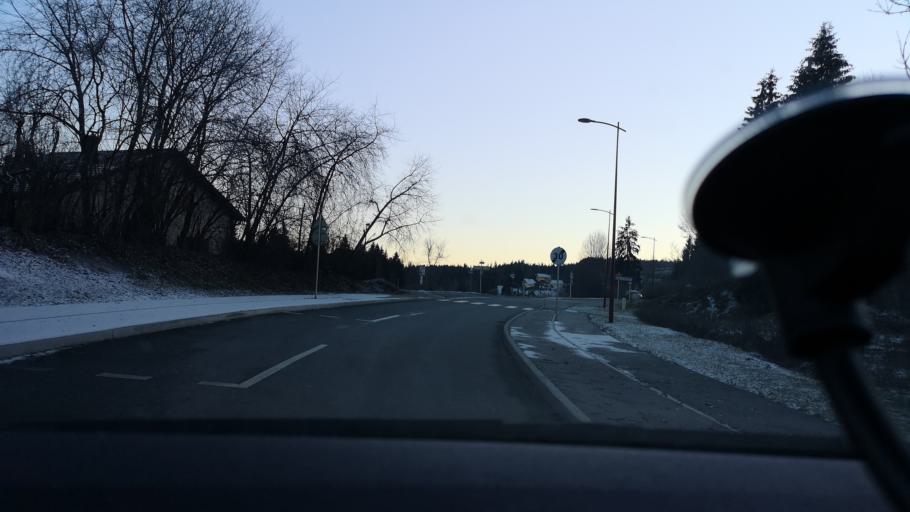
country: FR
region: Franche-Comte
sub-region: Departement du Doubs
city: Pontarlier
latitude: 46.8542
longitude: 6.3360
